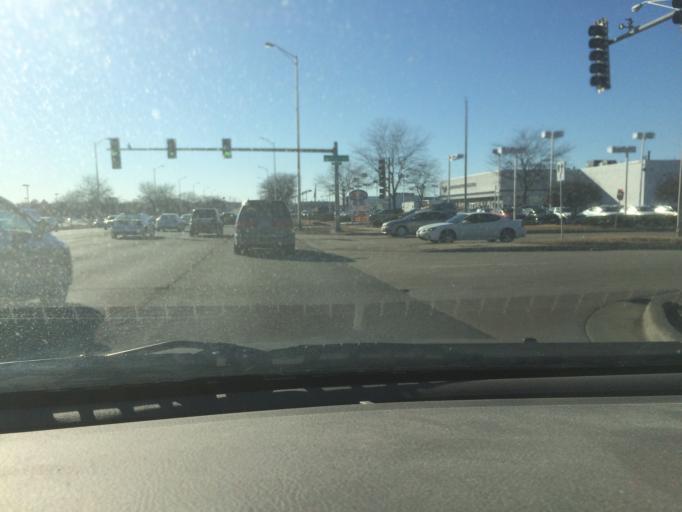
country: US
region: Illinois
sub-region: Cook County
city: Hoffman Estates
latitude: 42.0504
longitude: -88.0498
